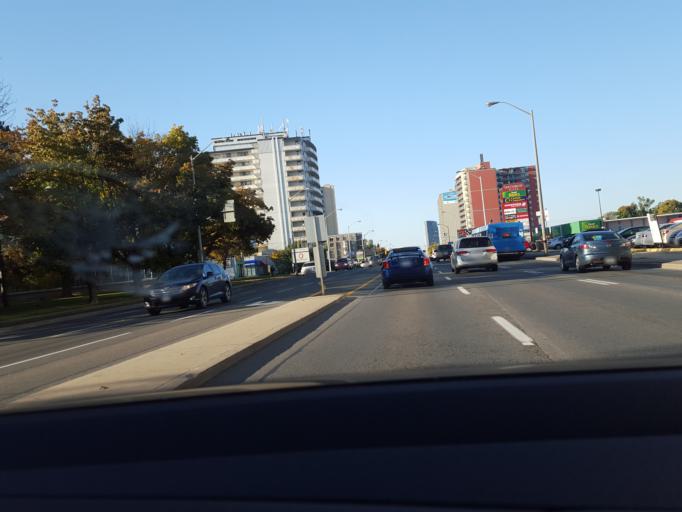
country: CA
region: Ontario
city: North York
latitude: 43.7847
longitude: -79.4167
